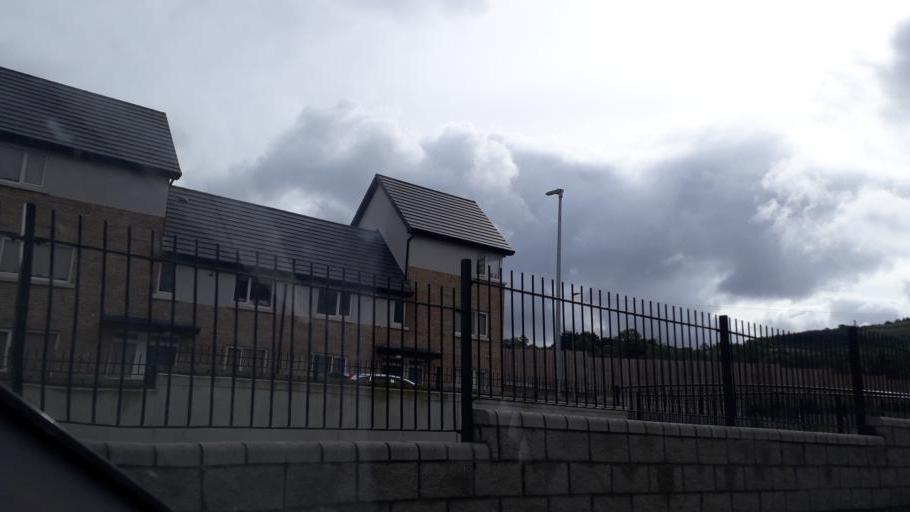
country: IE
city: Knocklyon
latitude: 53.2691
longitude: -6.3266
